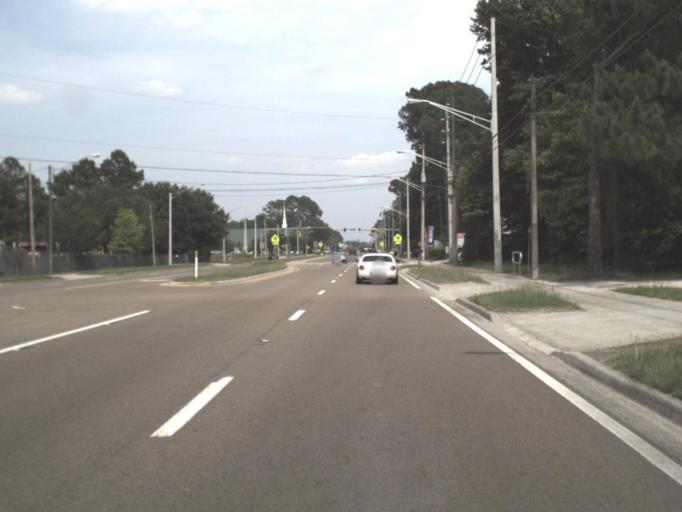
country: US
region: Florida
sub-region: Clay County
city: Bellair-Meadowbrook Terrace
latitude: 30.2474
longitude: -81.8260
